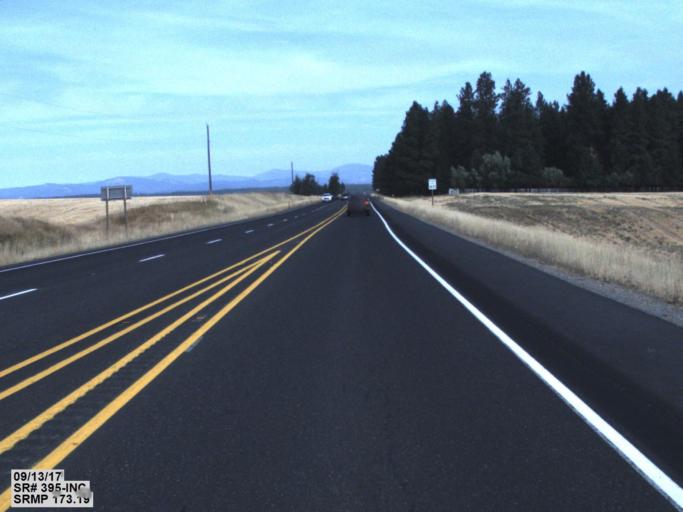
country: US
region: Washington
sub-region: Spokane County
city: Fairwood
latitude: 47.8616
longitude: -117.4219
